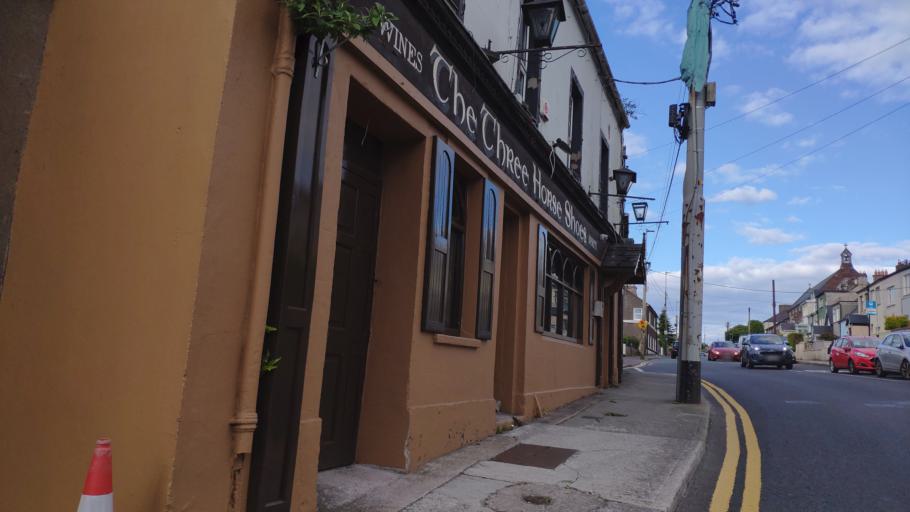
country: IE
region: Munster
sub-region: County Cork
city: Cork
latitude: 51.9097
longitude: -8.4507
